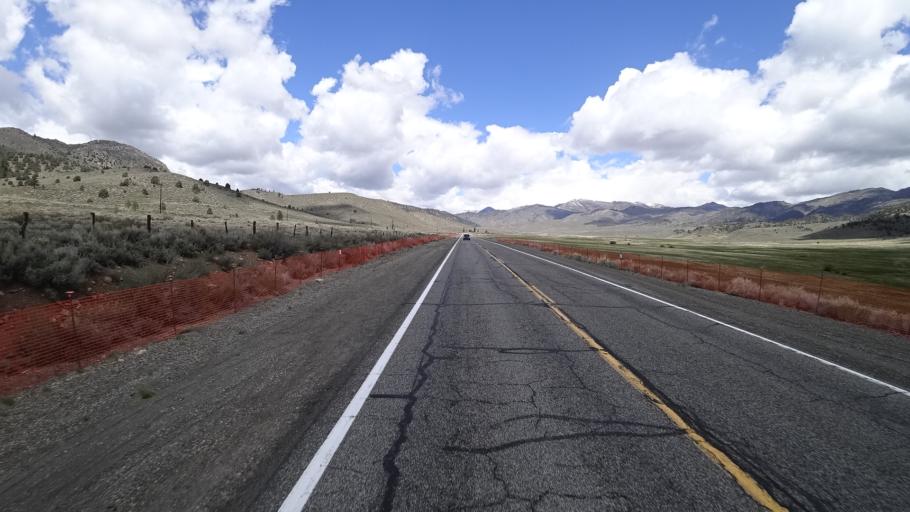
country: US
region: California
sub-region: Mono County
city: Bridgeport
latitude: 38.2976
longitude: -119.3112
